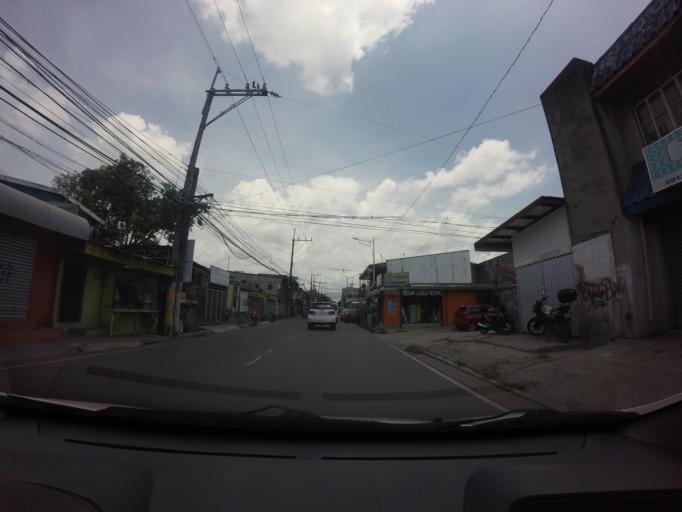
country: PH
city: Sambayanihan People's Village
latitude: 14.4290
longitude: 121.0146
